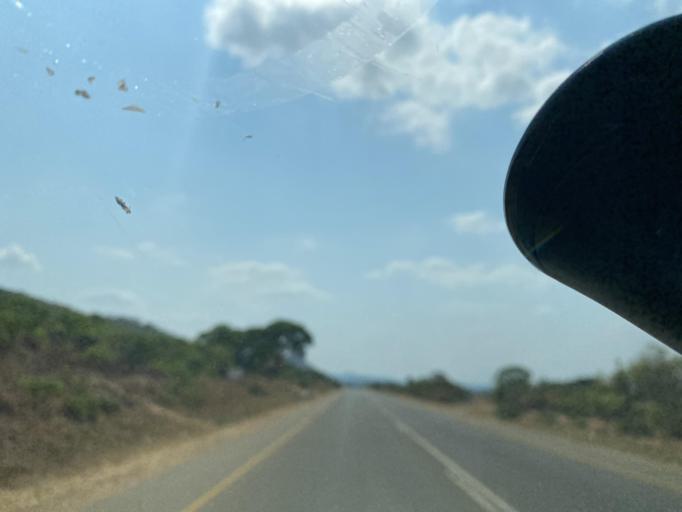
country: ZM
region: Lusaka
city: Chongwe
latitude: -15.6008
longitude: 28.7320
